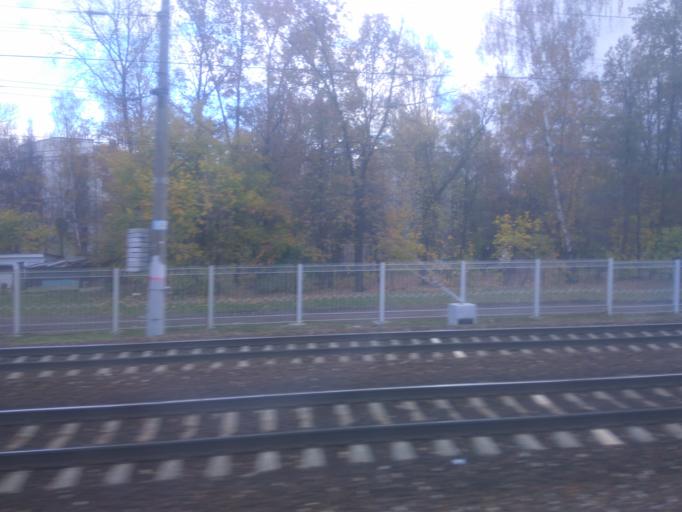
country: RU
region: Moscow
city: Mikhalkovo
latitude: 55.6644
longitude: 37.4169
